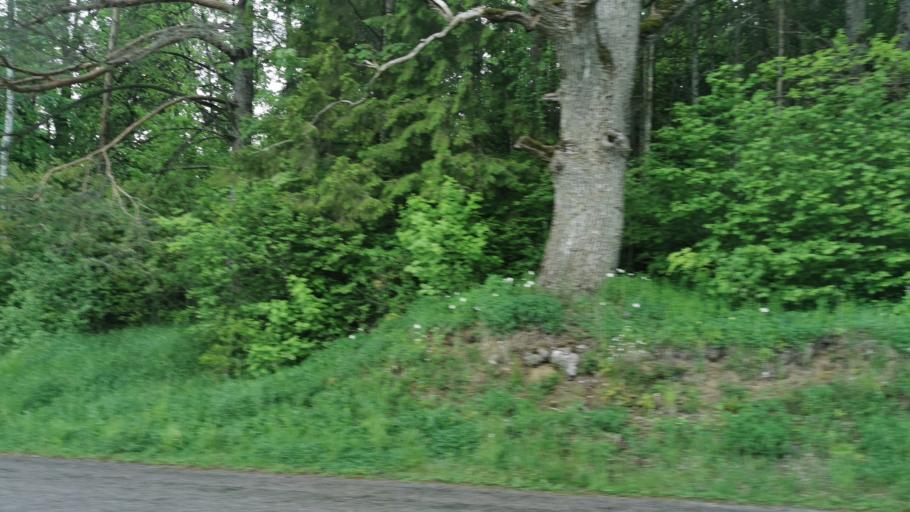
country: EE
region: Laeaene-Virumaa
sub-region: Rakvere linn
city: Rakvere
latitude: 59.2696
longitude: 26.3540
